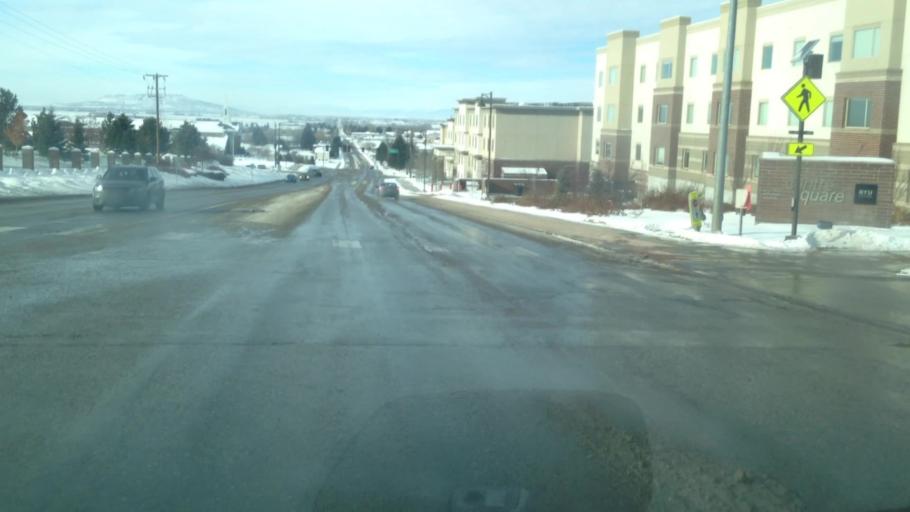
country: US
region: Idaho
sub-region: Madison County
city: Rexburg
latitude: 43.8116
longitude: -111.7866
